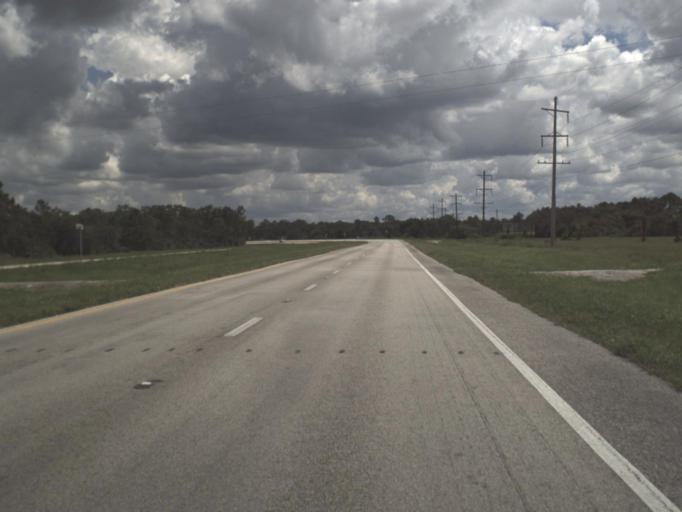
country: US
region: Florida
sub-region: Polk County
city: Babson Park
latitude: 27.8097
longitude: -81.3213
